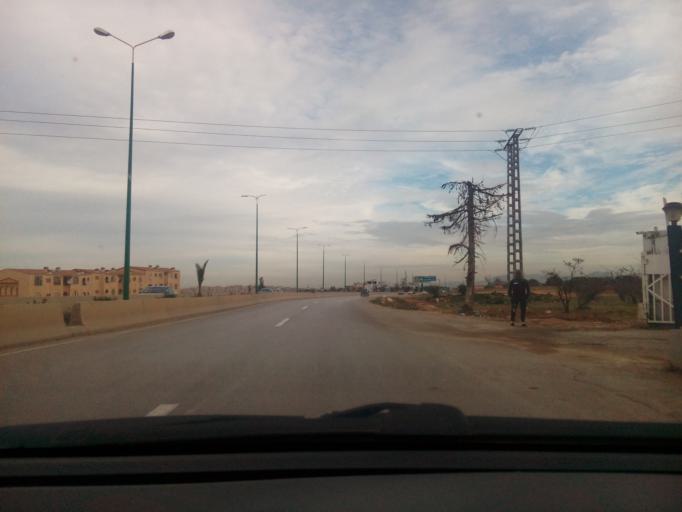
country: DZ
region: Tlemcen
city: Tlemcen
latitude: 34.9076
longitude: -1.3418
